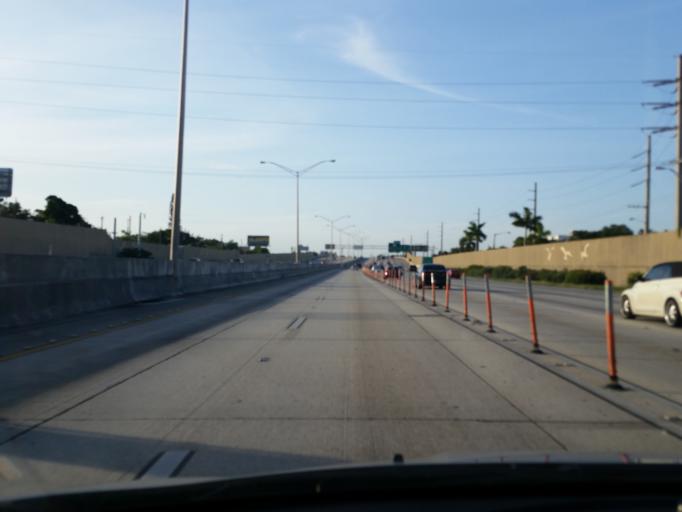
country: US
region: Florida
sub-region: Miami-Dade County
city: El Portal
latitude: 25.8354
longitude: -80.2060
